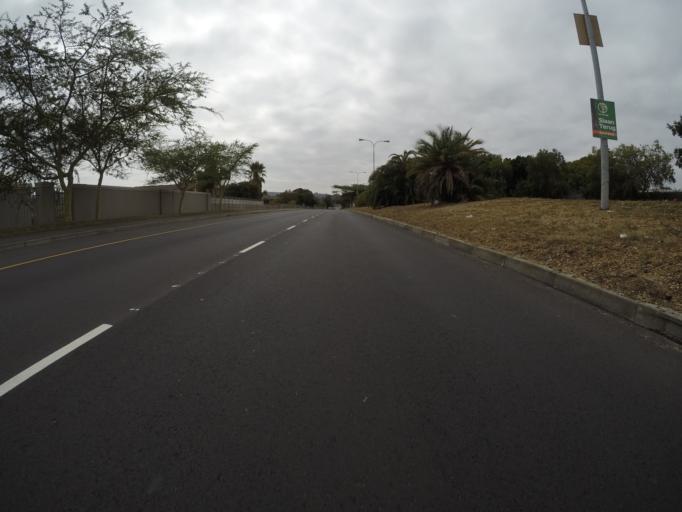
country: ZA
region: Western Cape
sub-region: City of Cape Town
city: Kraaifontein
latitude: -33.8670
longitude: 18.6330
